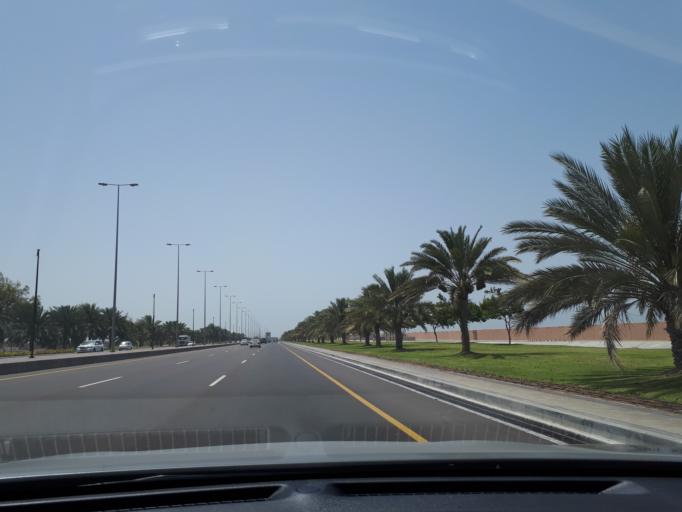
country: OM
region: Muhafazat Masqat
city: As Sib al Jadidah
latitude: 23.6872
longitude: 58.0910
